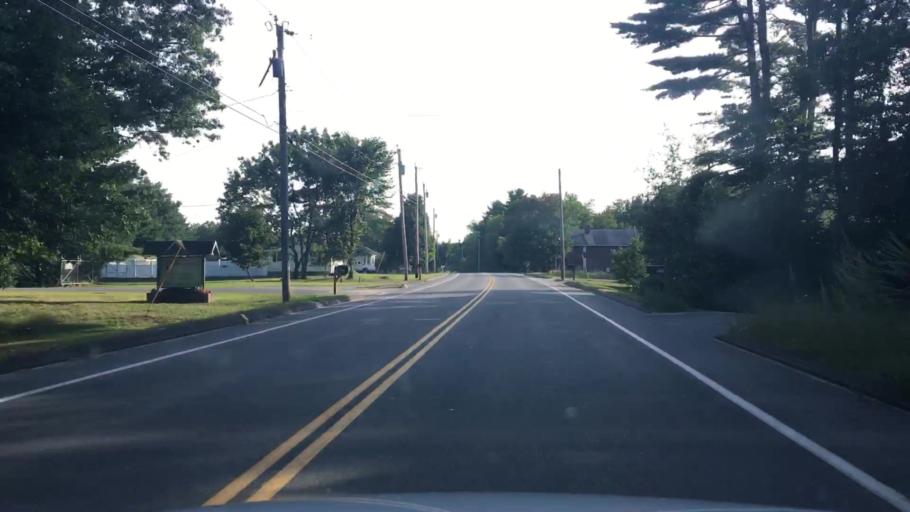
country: US
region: Maine
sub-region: Cumberland County
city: North Windham
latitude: 43.8207
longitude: -70.4399
